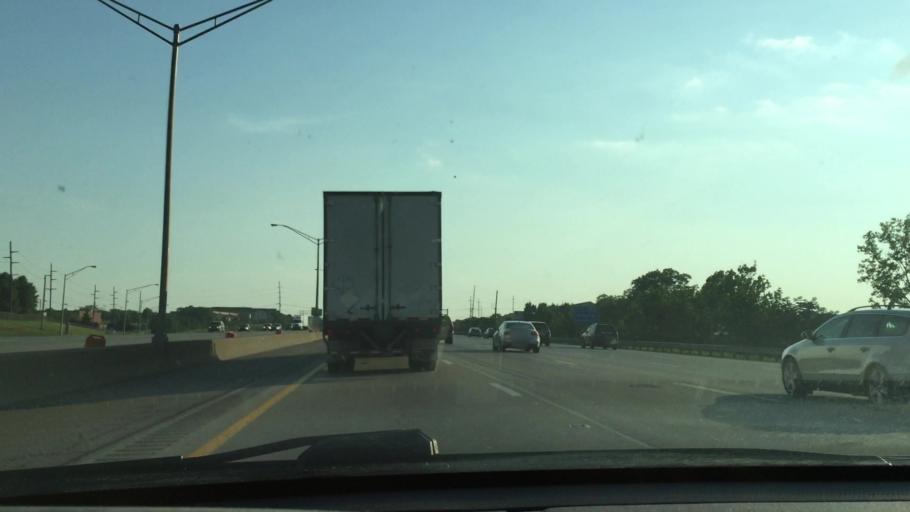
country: US
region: Kentucky
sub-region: Boone County
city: Florence
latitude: 39.0159
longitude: -84.6272
